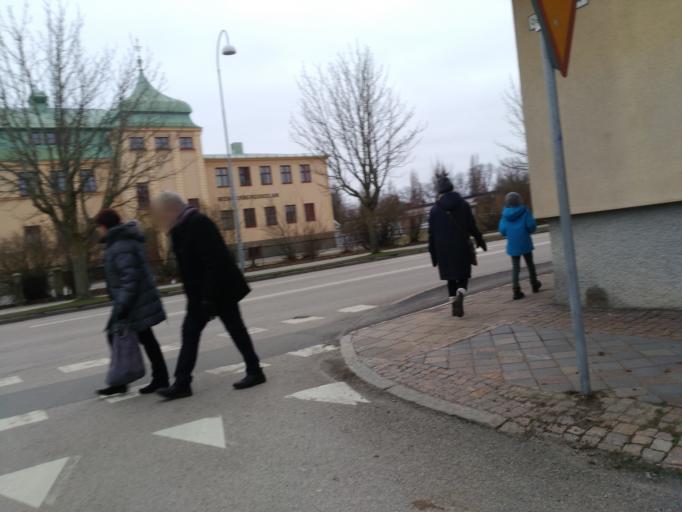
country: SE
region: Vaestra Goetaland
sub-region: Lidkopings Kommun
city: Lidkoping
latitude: 58.5001
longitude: 13.1612
